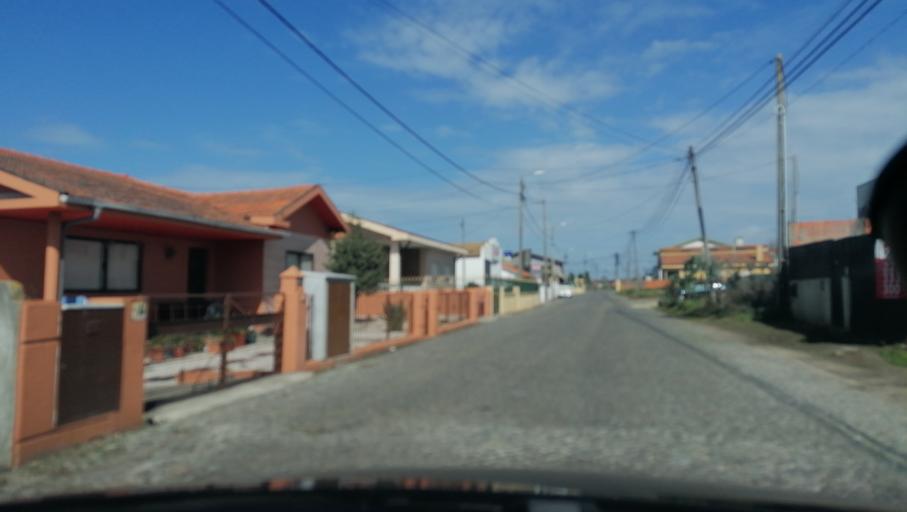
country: PT
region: Aveiro
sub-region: Espinho
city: Silvalde
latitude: 40.9913
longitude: -8.6368
